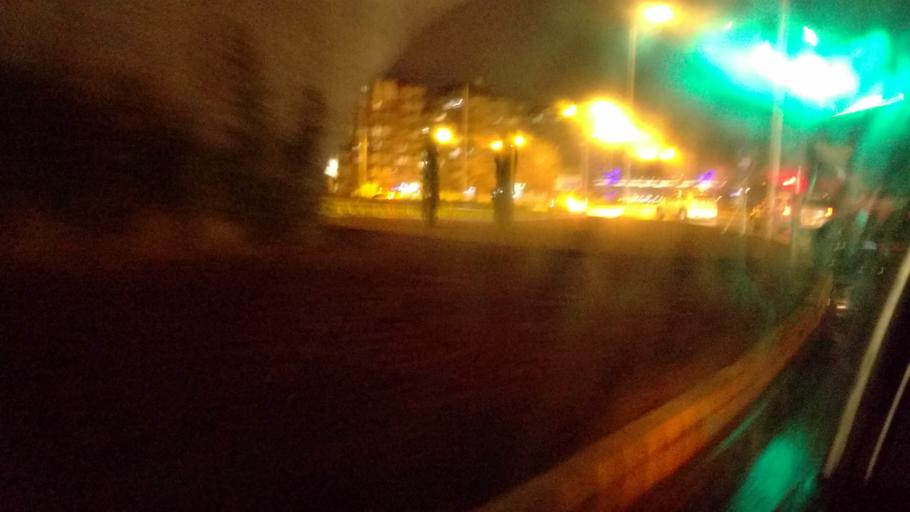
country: TR
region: Antalya
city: Antalya
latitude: 36.9063
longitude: 30.6819
